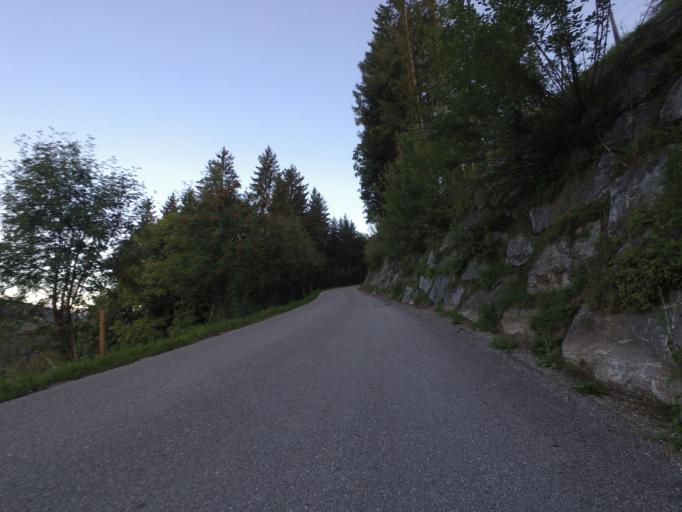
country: AT
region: Salzburg
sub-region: Politischer Bezirk Sankt Johann im Pongau
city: Goldegg
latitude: 47.3357
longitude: 13.1126
